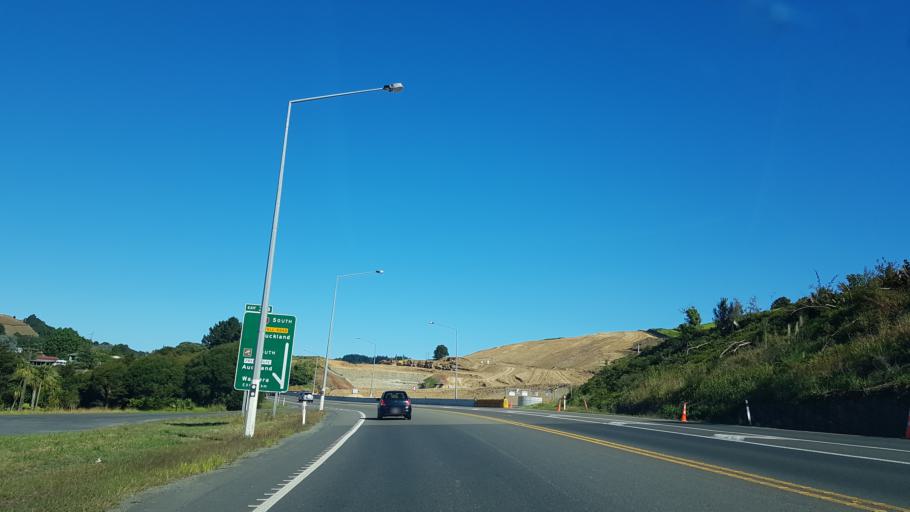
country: NZ
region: Auckland
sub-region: Auckland
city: Warkworth
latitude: -36.5162
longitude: 174.6695
